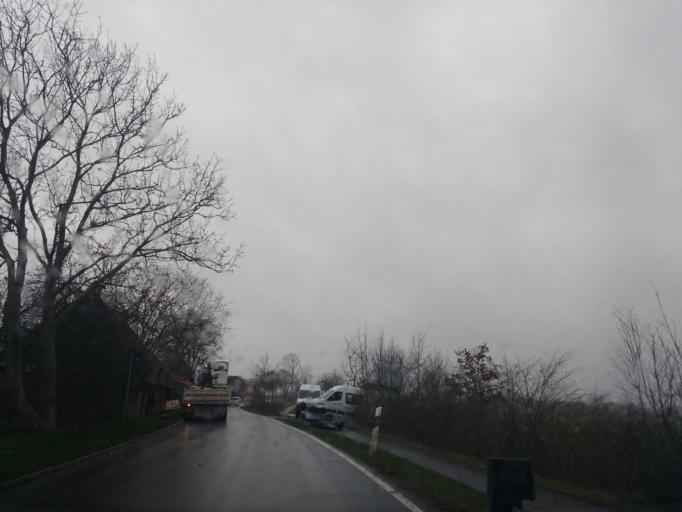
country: DE
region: Schleswig-Holstein
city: Gremersdorf
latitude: 54.3129
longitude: 10.9406
